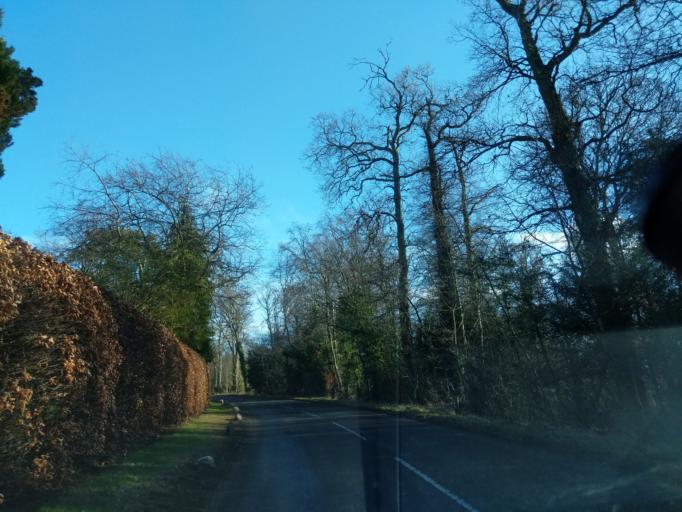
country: GB
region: Scotland
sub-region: East Lothian
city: Haddington
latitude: 55.9575
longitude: -2.7394
